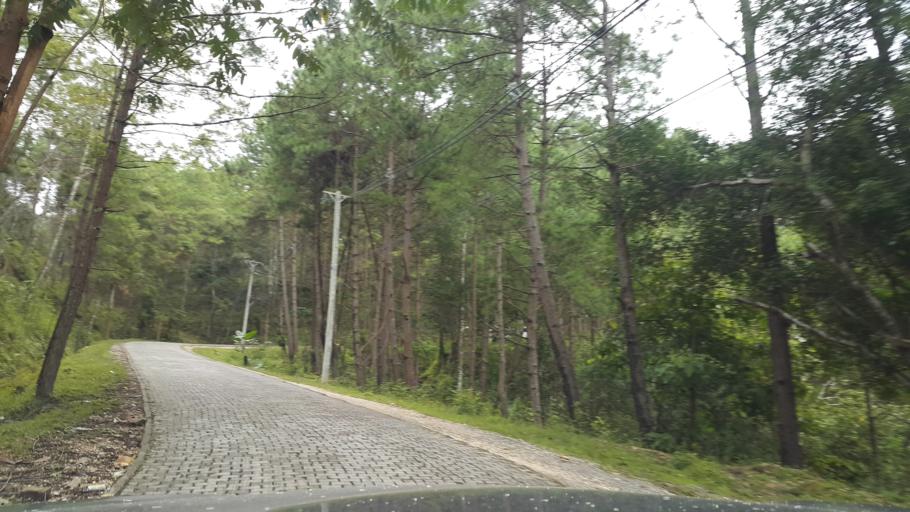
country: TH
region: Chiang Mai
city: Samoeng
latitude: 18.8884
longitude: 98.5296
